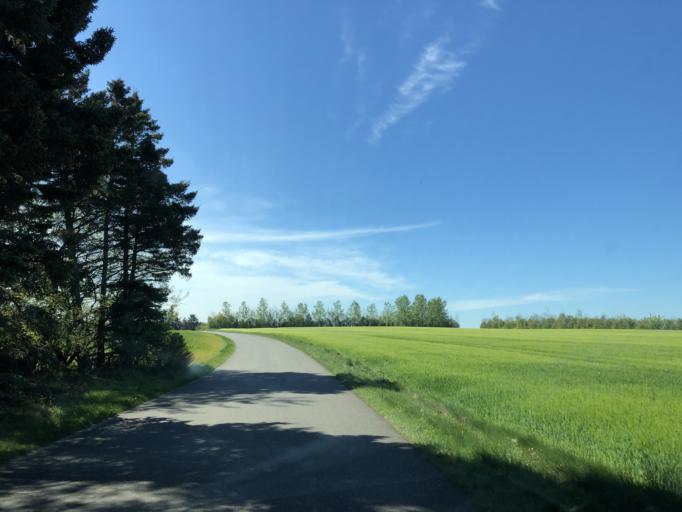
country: DK
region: Central Jutland
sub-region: Ringkobing-Skjern Kommune
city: Videbaek
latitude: 56.1985
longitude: 8.5120
